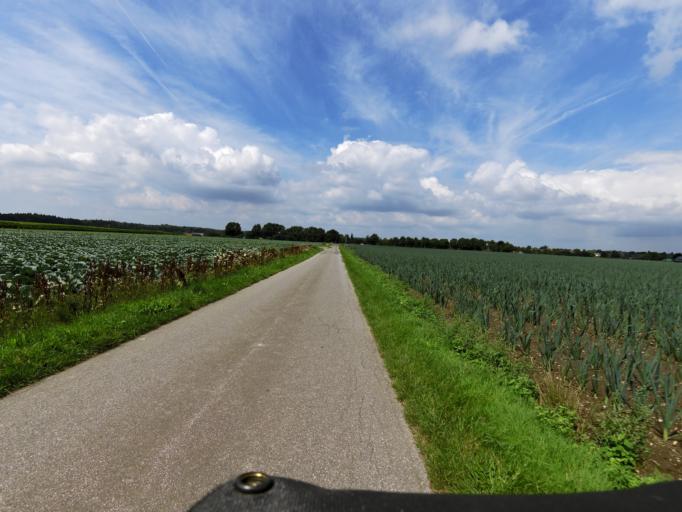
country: DE
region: North Rhine-Westphalia
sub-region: Regierungsbezirk Dusseldorf
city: Niederkruchten
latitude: 51.1854
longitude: 6.2029
